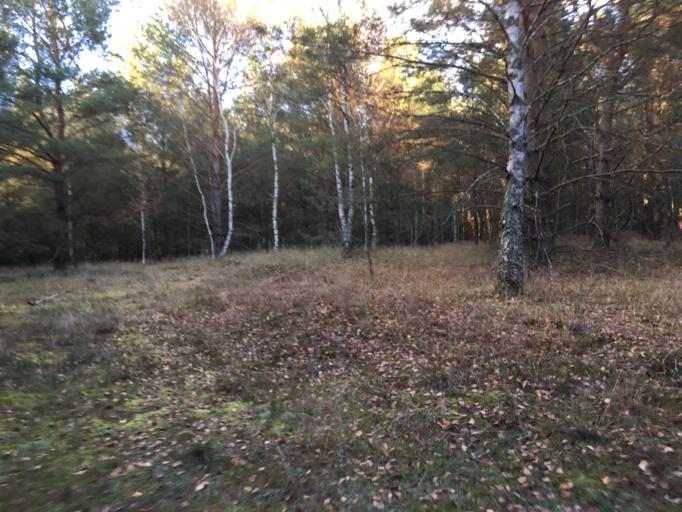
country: DE
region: Brandenburg
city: Birkenwerder
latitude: 52.7053
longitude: 13.3391
